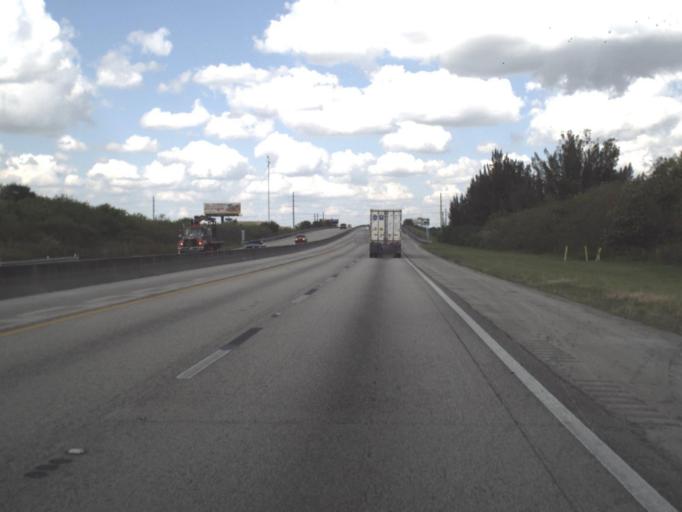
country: US
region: Florida
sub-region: Saint Lucie County
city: Fort Pierce South
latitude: 27.3746
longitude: -80.3840
